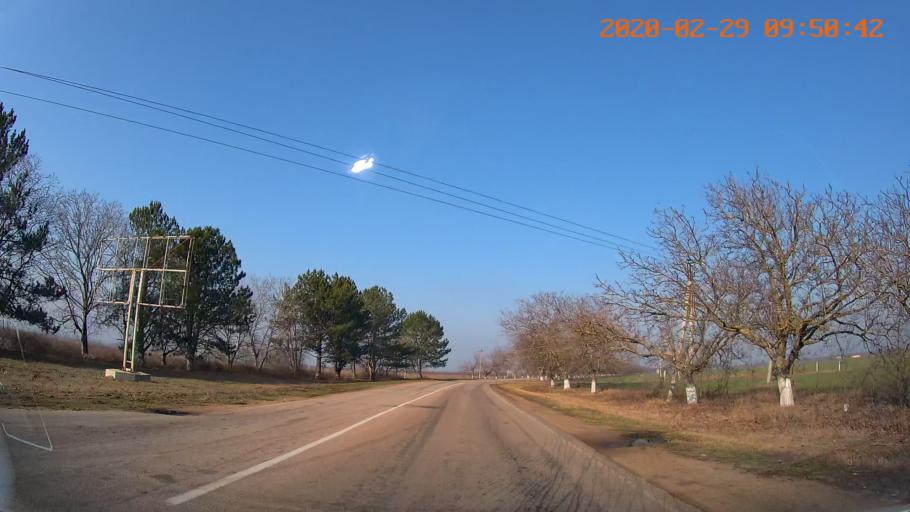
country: MD
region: Telenesti
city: Slobozia
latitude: 46.7030
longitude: 29.7511
